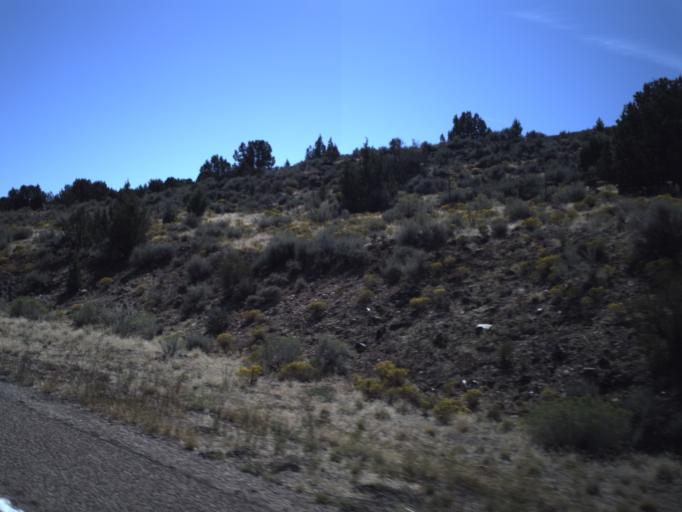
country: US
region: Utah
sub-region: Washington County
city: Ivins
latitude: 37.3212
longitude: -113.6901
